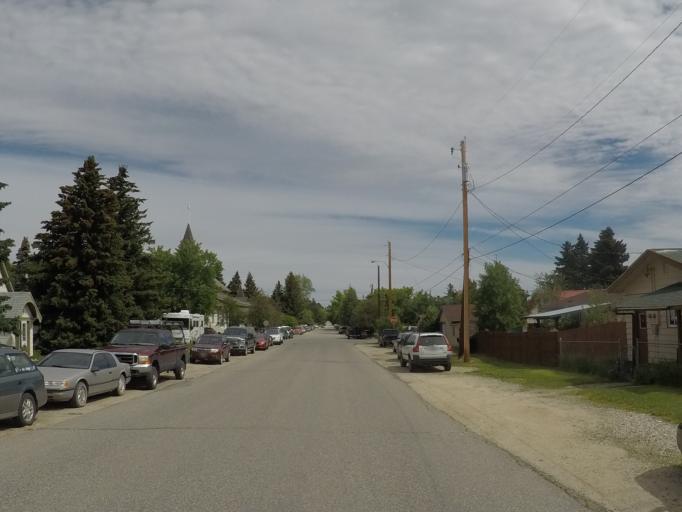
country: US
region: Montana
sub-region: Carbon County
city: Red Lodge
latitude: 45.1862
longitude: -109.2498
